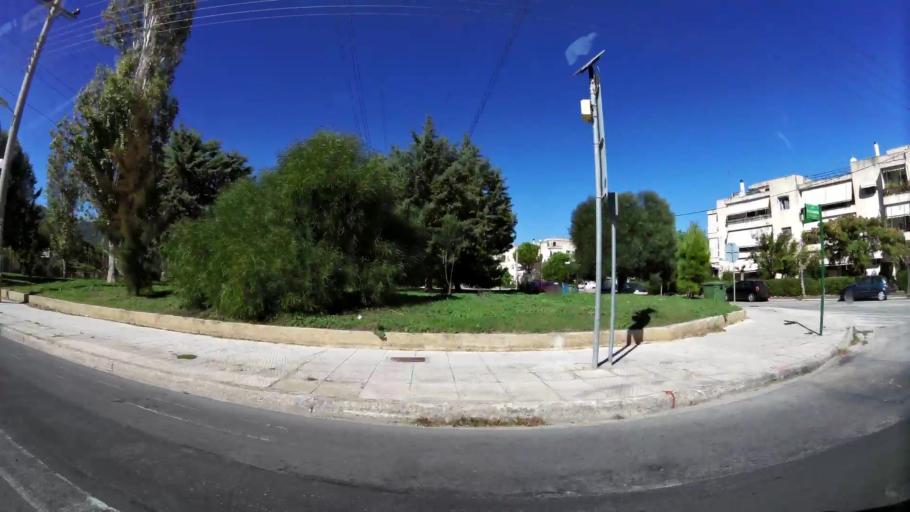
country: GR
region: Attica
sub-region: Nomarchia Anatolikis Attikis
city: Pallini
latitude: 37.9906
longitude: 23.8696
